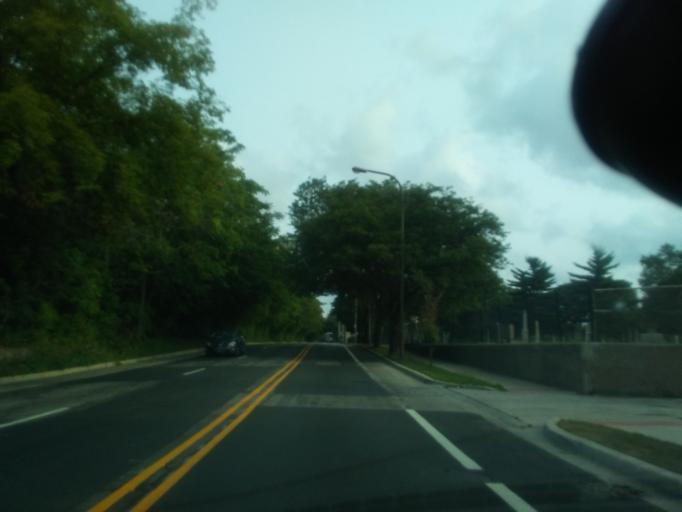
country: US
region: Illinois
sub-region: Cook County
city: Evanston
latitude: 42.0229
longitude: -87.6772
